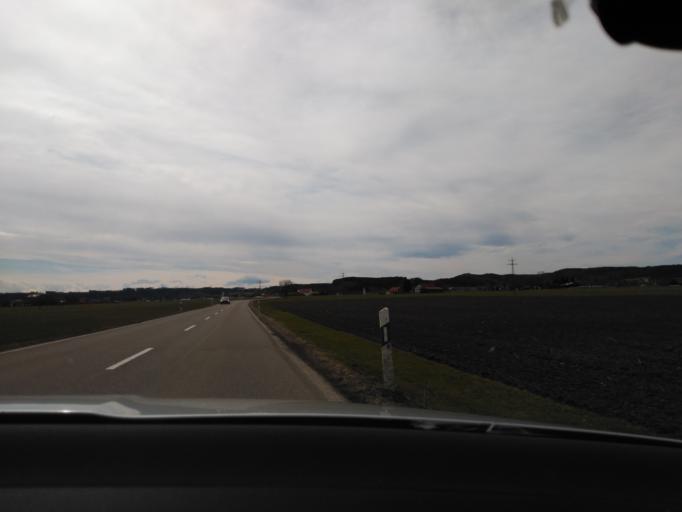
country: DE
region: Baden-Wuerttemberg
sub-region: Tuebingen Region
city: Aitrach
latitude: 47.9141
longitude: 10.0956
